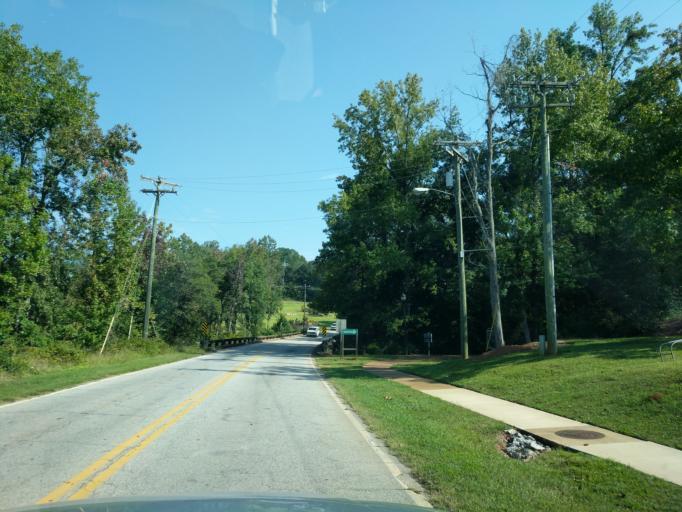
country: US
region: South Carolina
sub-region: Spartanburg County
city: Lyman
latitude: 34.9393
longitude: -82.1237
